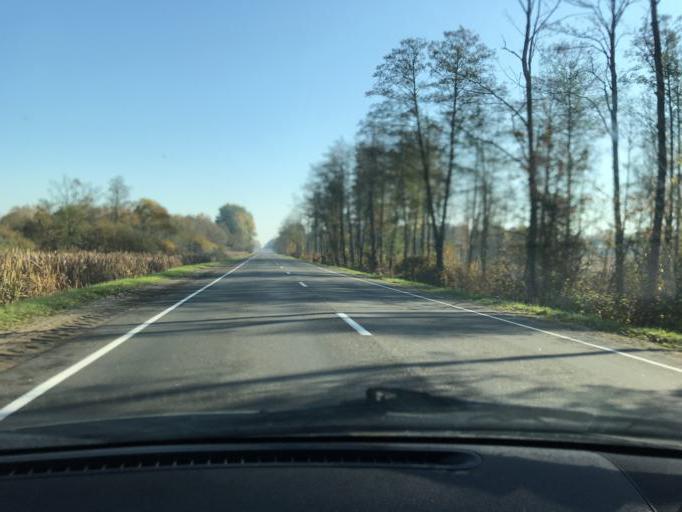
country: BY
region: Brest
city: Lyakhavichy
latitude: 52.9577
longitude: 26.3366
